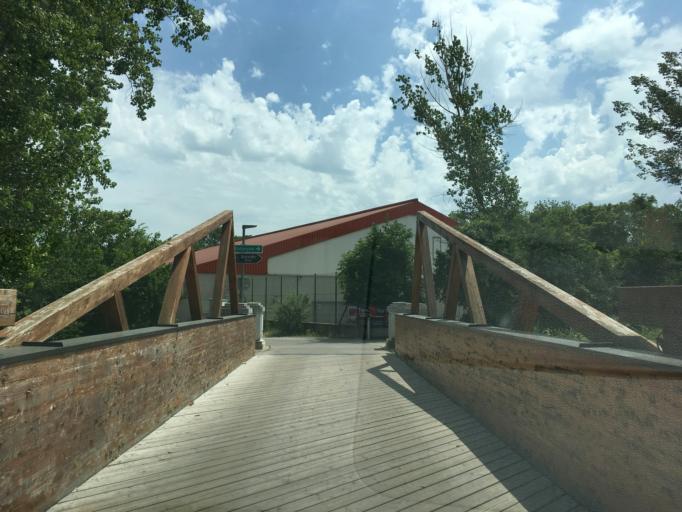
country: AT
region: Lower Austria
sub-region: Politischer Bezirk Baden
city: Tattendorf
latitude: 47.9590
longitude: 16.3052
